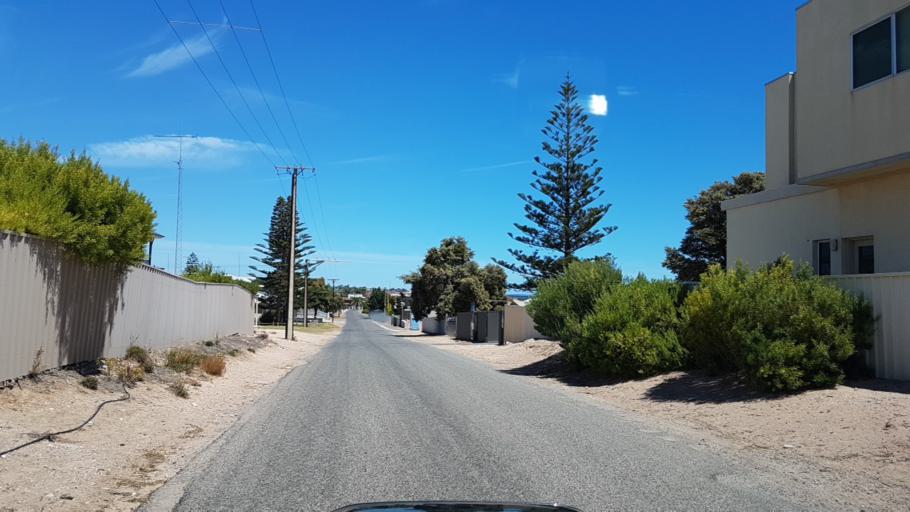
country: AU
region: South Australia
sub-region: Copper Coast
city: Wallaroo
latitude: -34.0563
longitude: 137.5623
